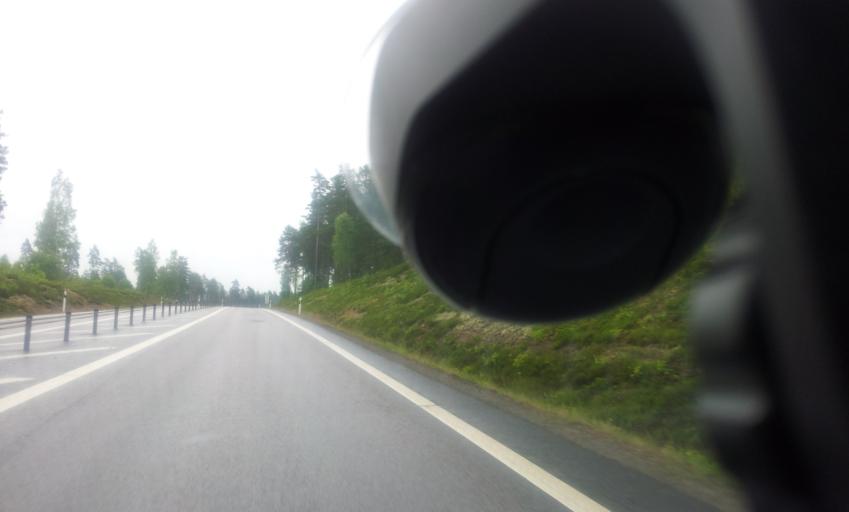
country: SE
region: Kalmar
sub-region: Vasterviks Kommun
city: Forserum
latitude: 58.0661
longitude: 16.5237
